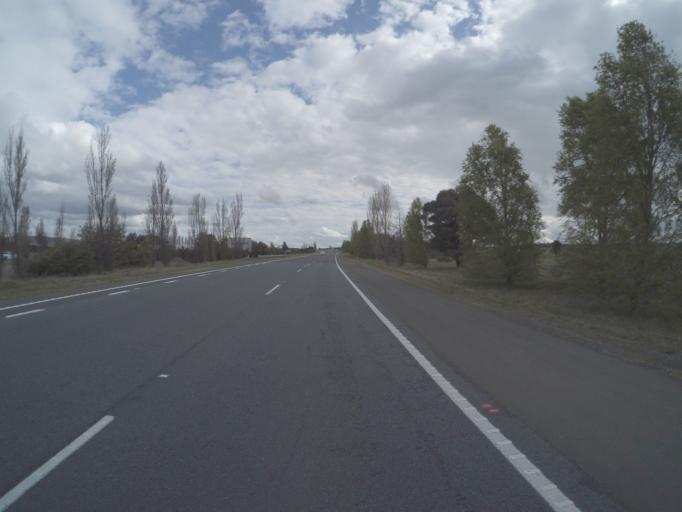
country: AU
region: New South Wales
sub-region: Goulburn Mulwaree
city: Goulburn
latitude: -34.7974
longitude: 149.6146
